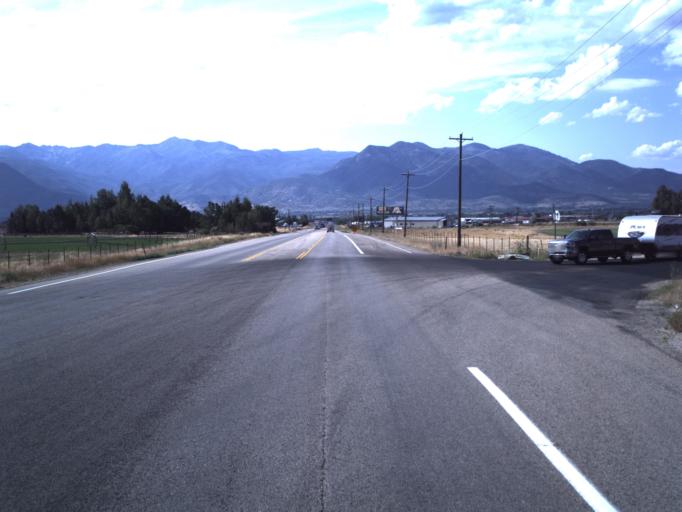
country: US
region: Utah
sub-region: Wasatch County
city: Heber
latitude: 40.4752
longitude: -111.3951
